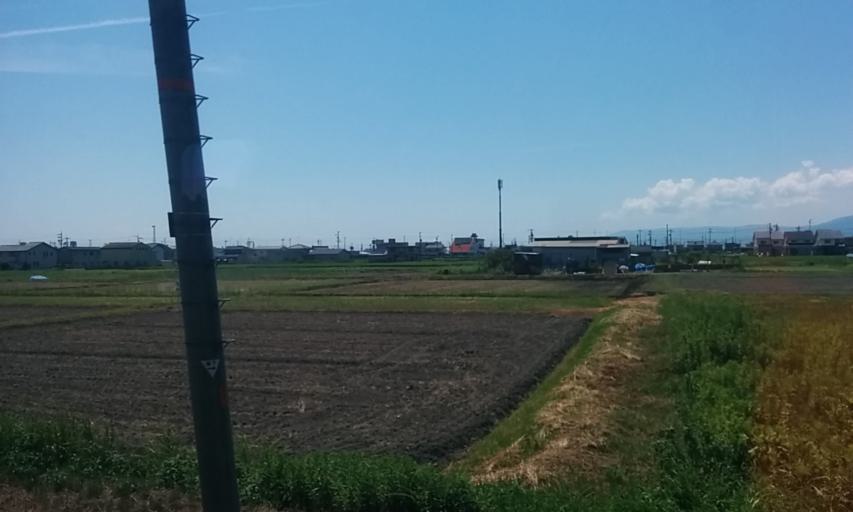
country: JP
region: Gifu
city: Tarui
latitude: 35.3709
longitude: 136.5591
